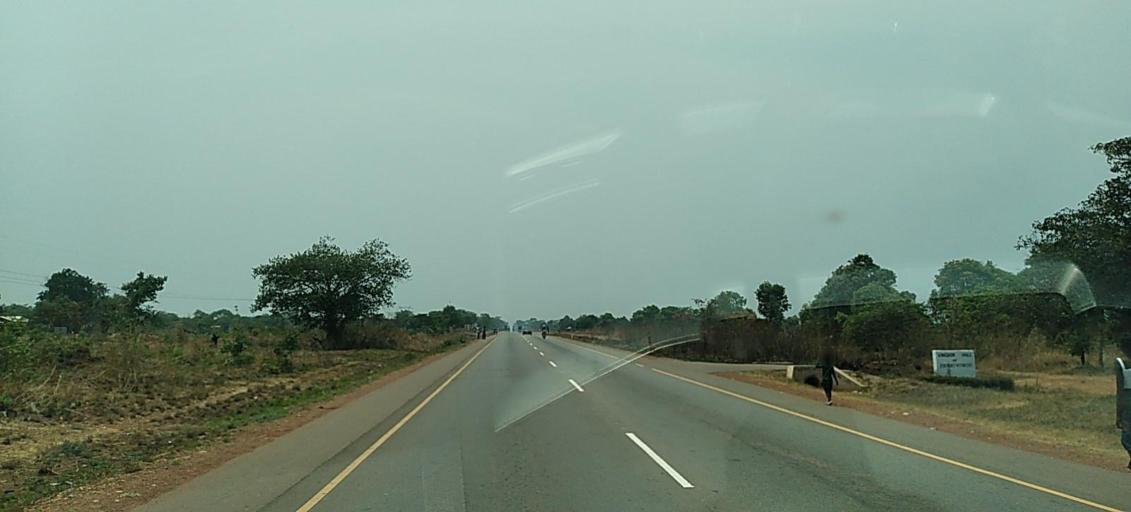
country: CD
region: Katanga
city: Kipushi
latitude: -12.3361
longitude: 27.0704
